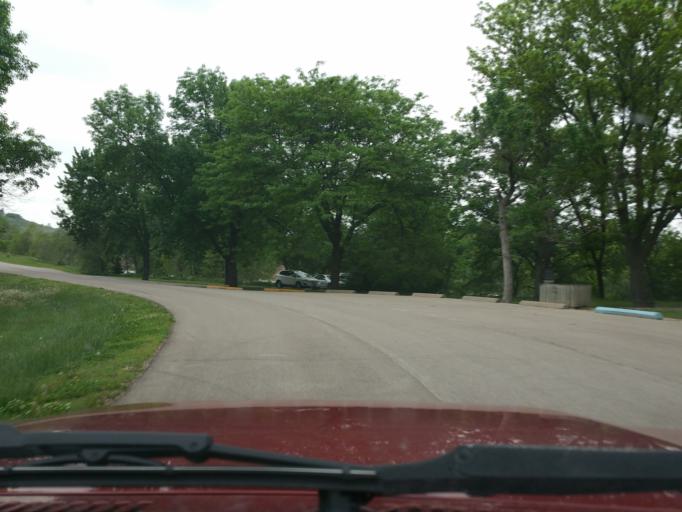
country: US
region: Kansas
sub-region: Riley County
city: Manhattan
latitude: 39.2470
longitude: -96.5936
